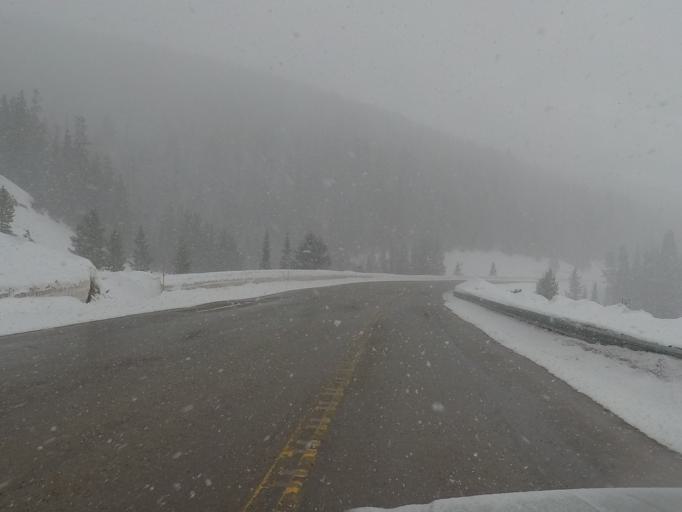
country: US
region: Montana
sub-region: Meagher County
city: White Sulphur Springs
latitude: 46.8343
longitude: -110.6954
